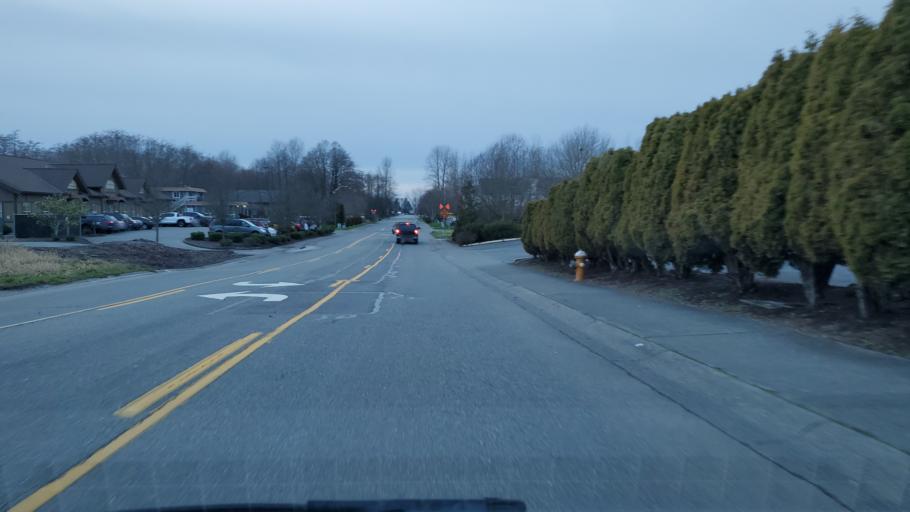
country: US
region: Washington
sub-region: Skagit County
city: Mount Vernon
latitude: 48.4339
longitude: -122.3201
